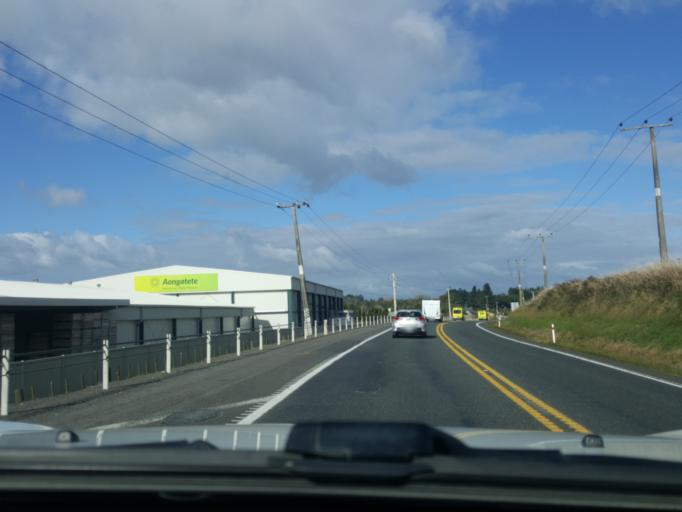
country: NZ
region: Bay of Plenty
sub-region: Western Bay of Plenty District
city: Katikati
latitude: -37.6093
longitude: 175.9445
